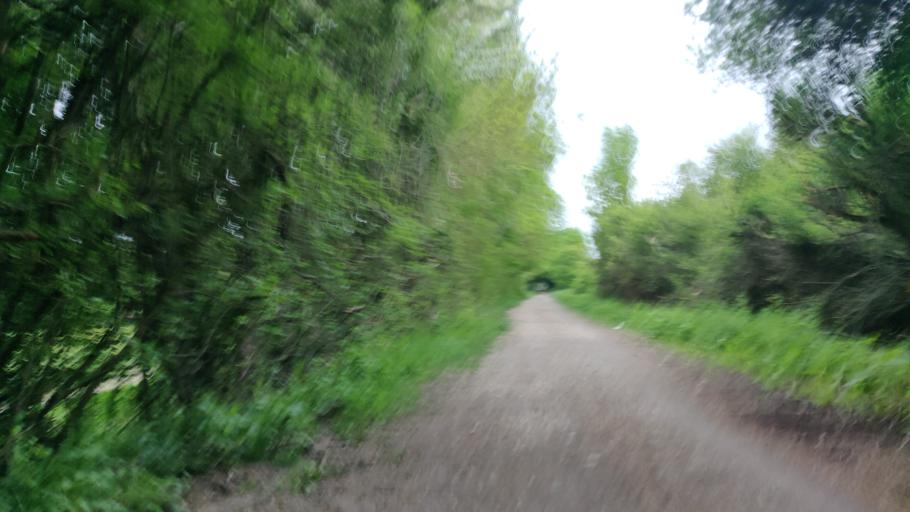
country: GB
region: England
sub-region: West Sussex
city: Partridge Green
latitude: 50.9988
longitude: -0.3189
